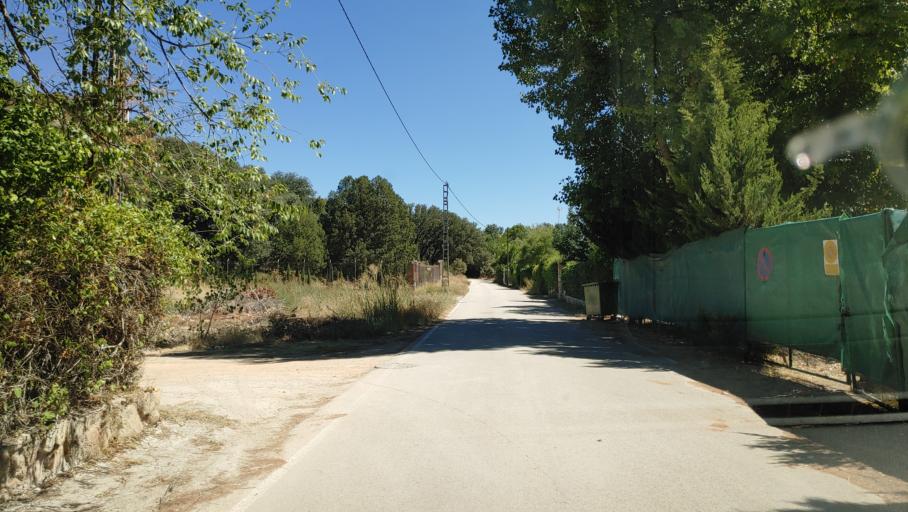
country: ES
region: Castille-La Mancha
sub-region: Provincia de Ciudad Real
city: Ruidera
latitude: 38.9271
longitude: -2.8277
